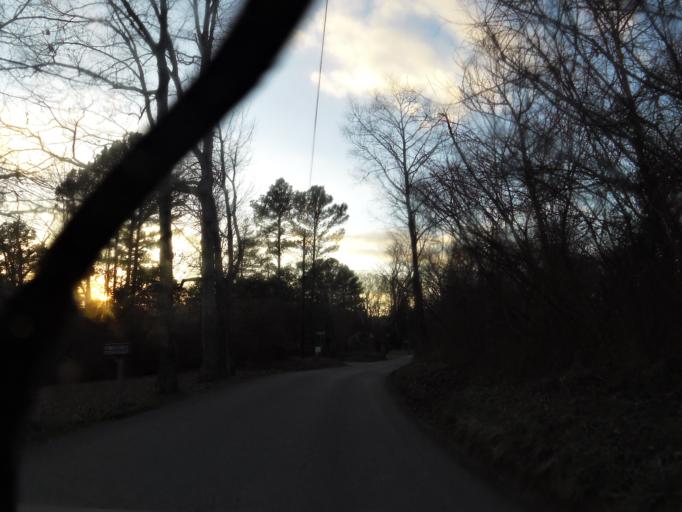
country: US
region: Tennessee
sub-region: Knox County
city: Knoxville
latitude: 35.9163
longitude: -83.9410
